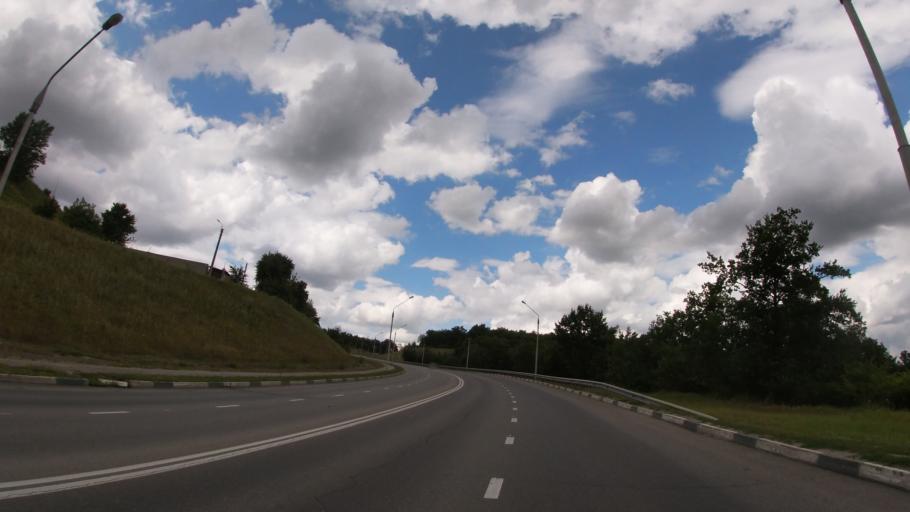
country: RU
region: Belgorod
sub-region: Belgorodskiy Rayon
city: Belgorod
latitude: 50.6203
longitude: 36.6162
